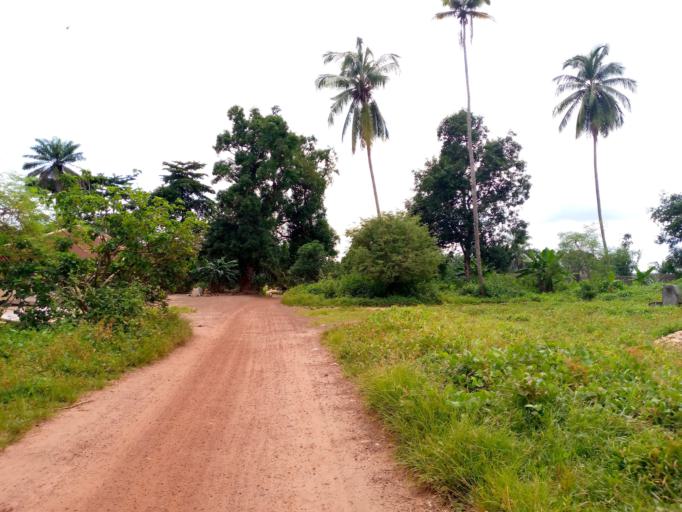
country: SL
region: Northern Province
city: Magburaka
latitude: 8.7096
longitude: -11.9294
